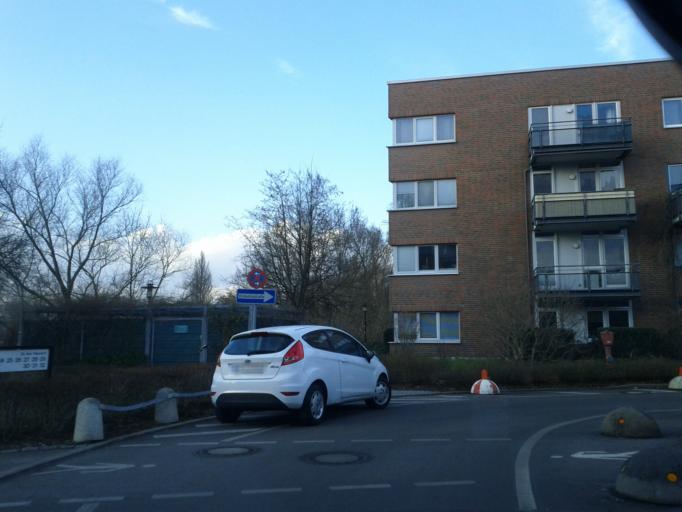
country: DE
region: Berlin
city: Berlin Koepenick
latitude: 52.4484
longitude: 13.5821
